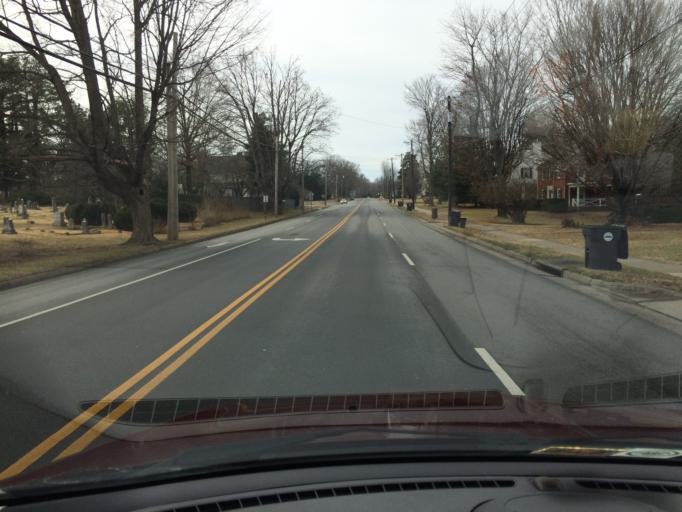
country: US
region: Virginia
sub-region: City of Bedford
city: Bedford
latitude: 37.3426
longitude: -79.5119
